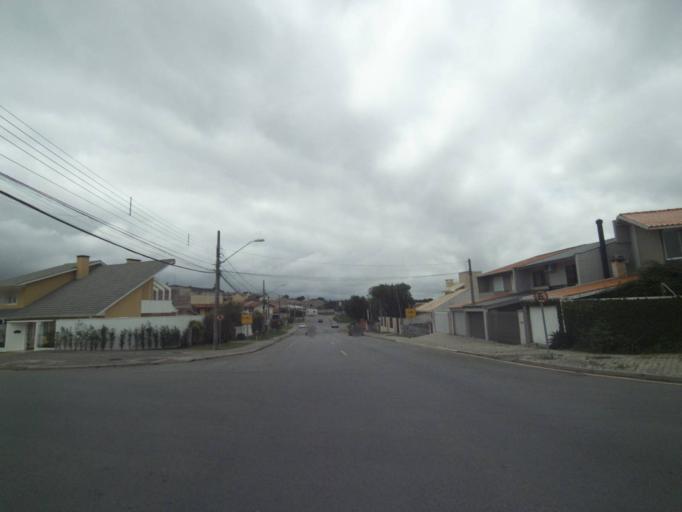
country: BR
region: Parana
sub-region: Pinhais
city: Pinhais
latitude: -25.4362
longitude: -49.2293
